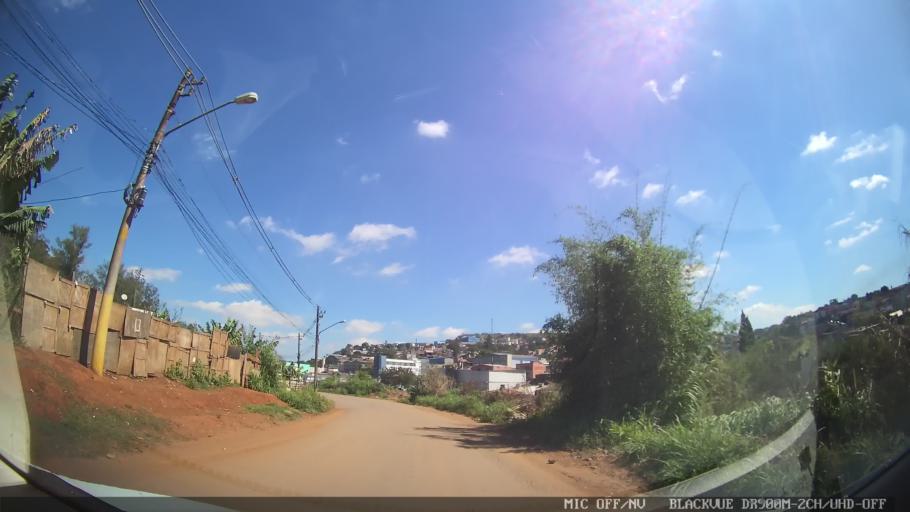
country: BR
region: Sao Paulo
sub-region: Cajamar
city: Cajamar
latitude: -23.4152
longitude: -46.8199
